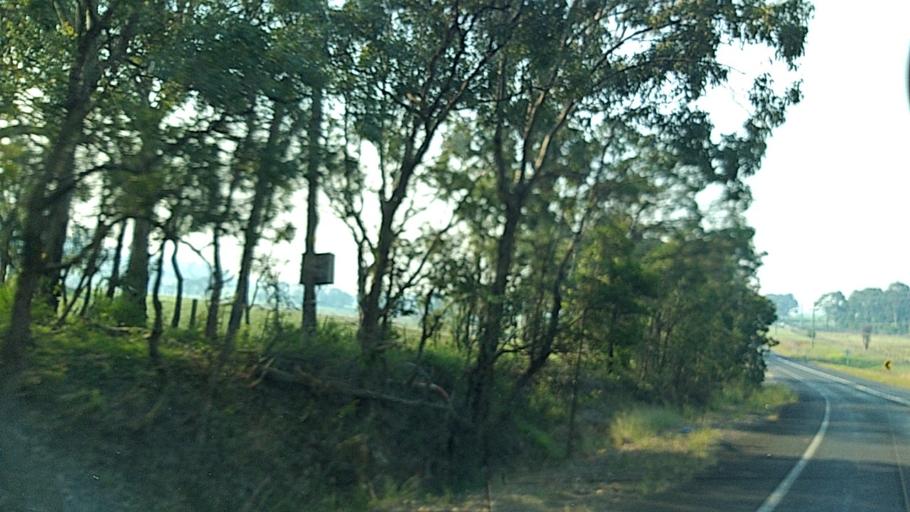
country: AU
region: New South Wales
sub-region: Wollondilly
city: Douglas Park
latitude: -34.2205
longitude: 150.7692
